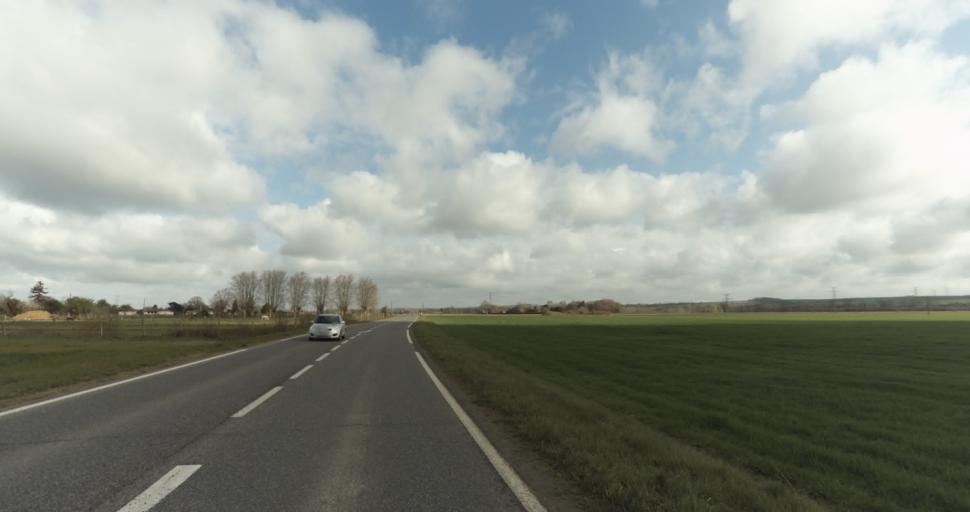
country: FR
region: Midi-Pyrenees
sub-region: Departement de la Haute-Garonne
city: Miremont
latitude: 43.3755
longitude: 1.4459
